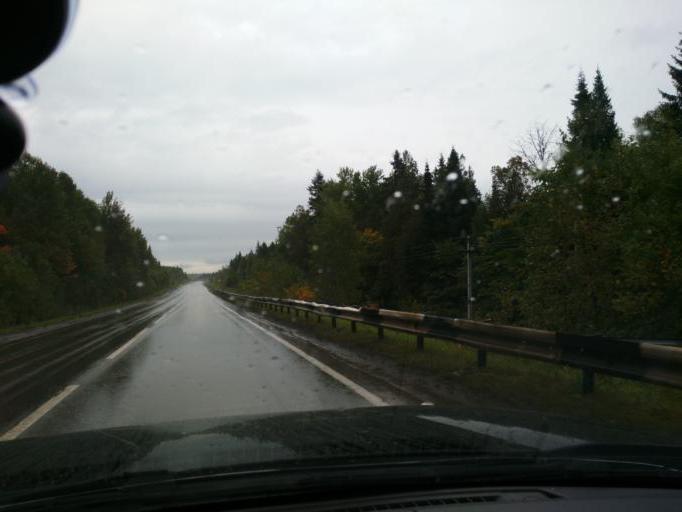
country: RU
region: Perm
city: Kultayevo
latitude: 57.8183
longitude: 55.7995
